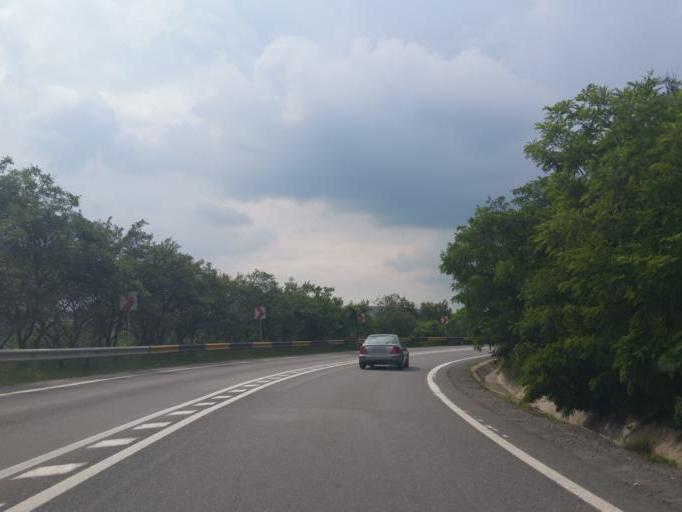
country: RO
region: Salaj
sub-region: Comuna Treznea
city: Treznea
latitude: 47.1252
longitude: 23.1306
